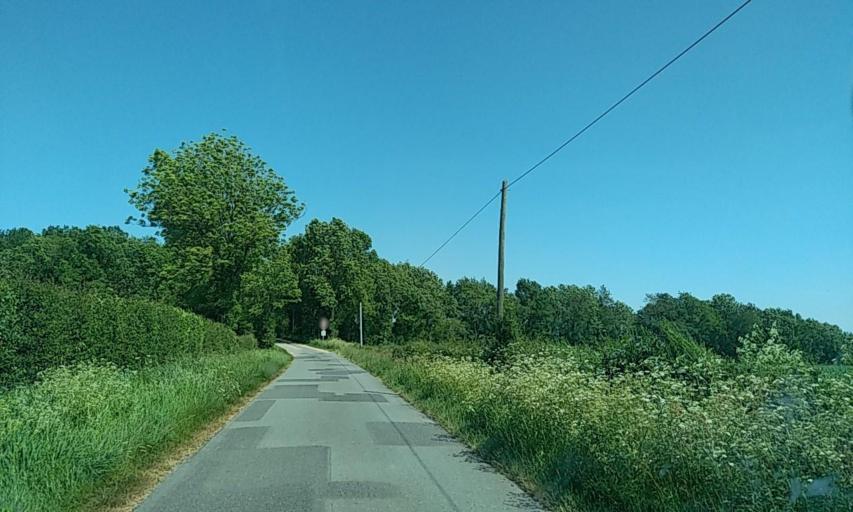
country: FR
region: Poitou-Charentes
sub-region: Departement des Deux-Sevres
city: La Chapelle-Saint-Laurent
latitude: 46.7702
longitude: -0.4762
